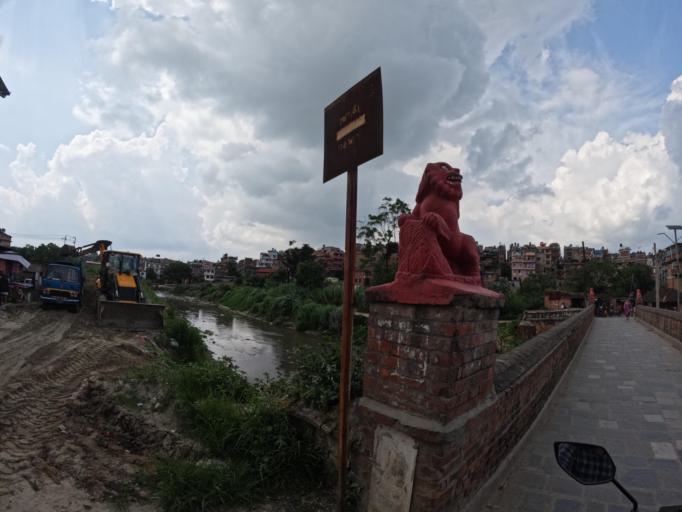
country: NP
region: Central Region
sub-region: Bagmati Zone
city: Bhaktapur
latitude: 27.6678
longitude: 85.4270
